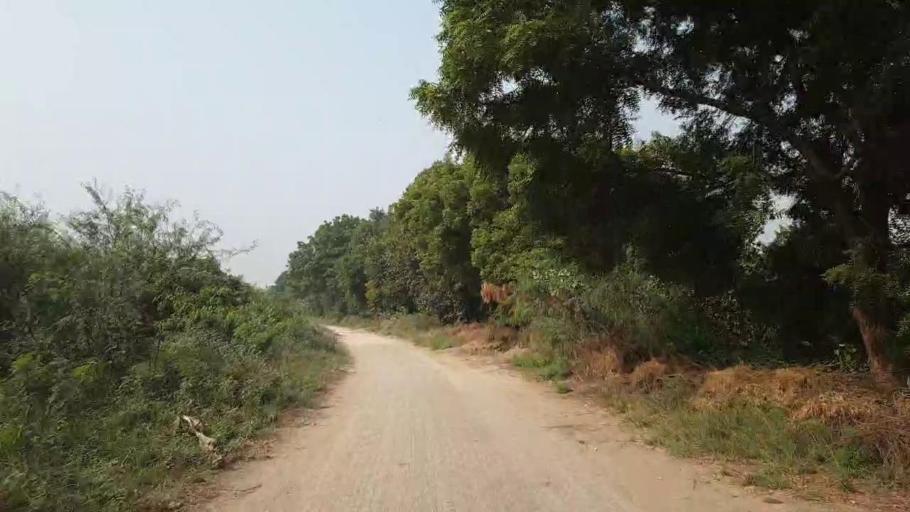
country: PK
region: Sindh
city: Tando Muhammad Khan
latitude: 25.1887
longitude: 68.5945
